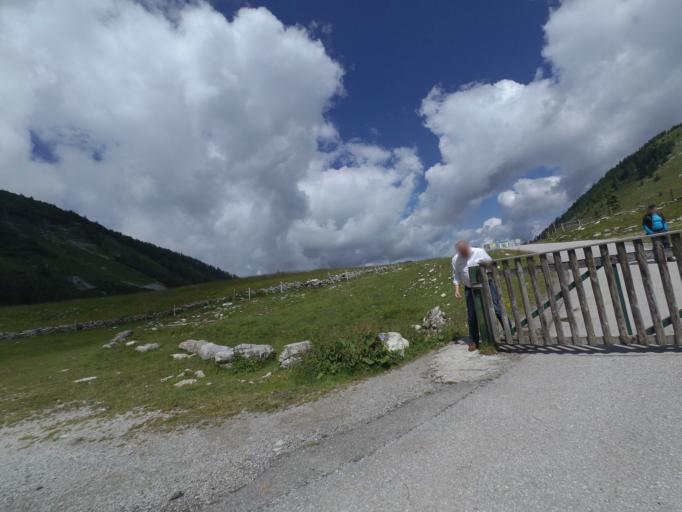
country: AT
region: Salzburg
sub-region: Politischer Bezirk Salzburg-Umgebung
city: Hintersee
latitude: 47.6490
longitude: 13.2825
